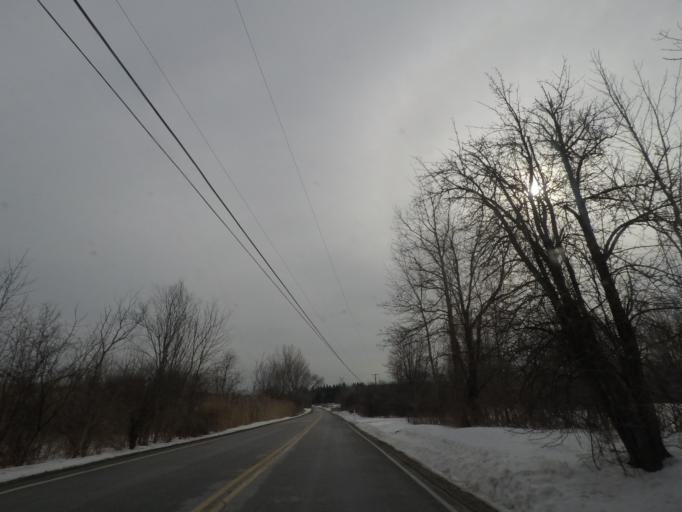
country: US
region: New York
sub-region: Albany County
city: Altamont
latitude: 42.6907
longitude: -73.9844
